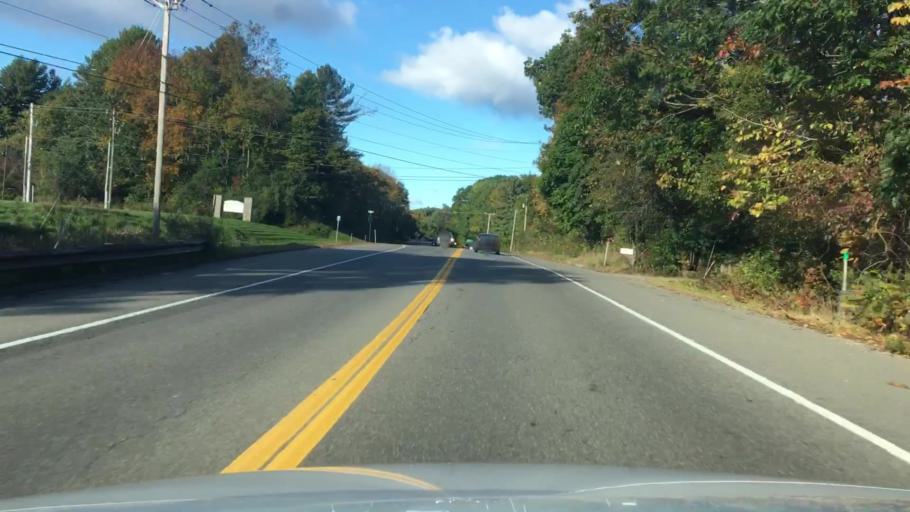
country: US
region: New Hampshire
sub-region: Strafford County
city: Durham
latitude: 43.1378
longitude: -70.9005
